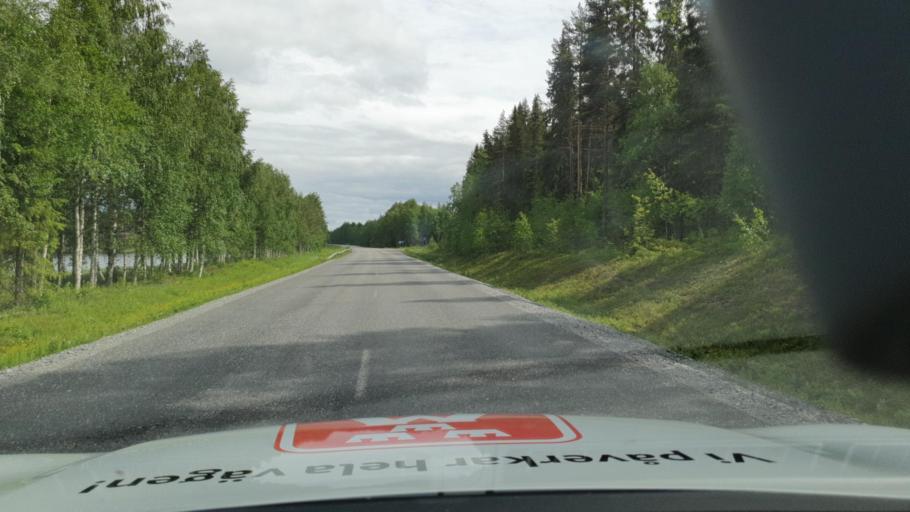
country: SE
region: Vaesterbotten
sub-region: Dorotea Kommun
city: Dorotea
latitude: 64.2339
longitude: 16.8025
